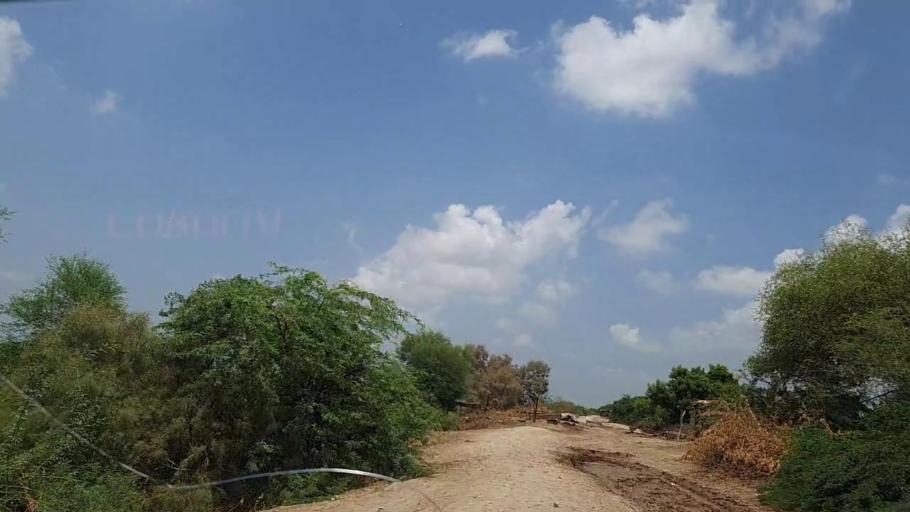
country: PK
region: Sindh
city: Tharu Shah
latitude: 26.9523
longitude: 68.0236
